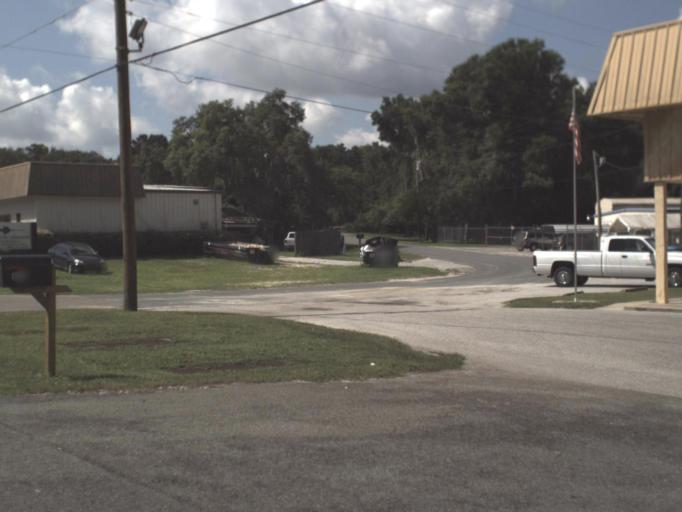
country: US
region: Florida
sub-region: Citrus County
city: Floral City
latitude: 28.7838
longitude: -82.2984
